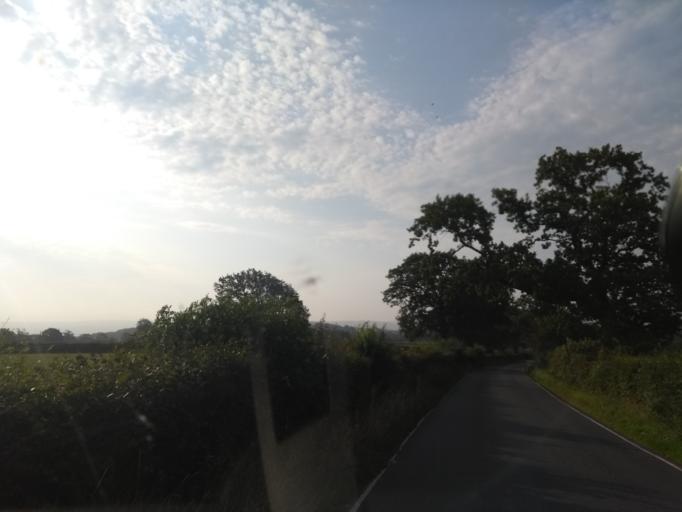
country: GB
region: England
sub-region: Devon
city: Colyton
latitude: 50.7961
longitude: -3.0966
